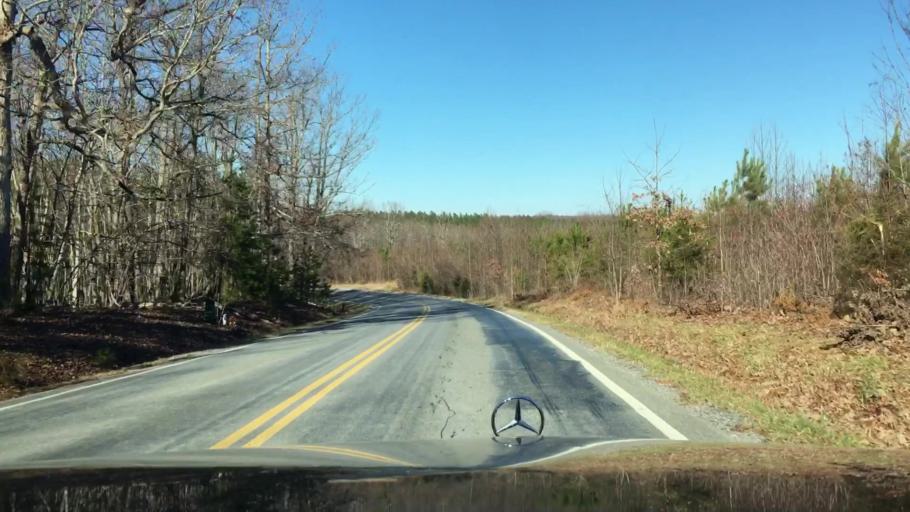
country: US
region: Virginia
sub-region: Pittsylvania County
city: Motley
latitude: 37.1676
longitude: -79.4053
